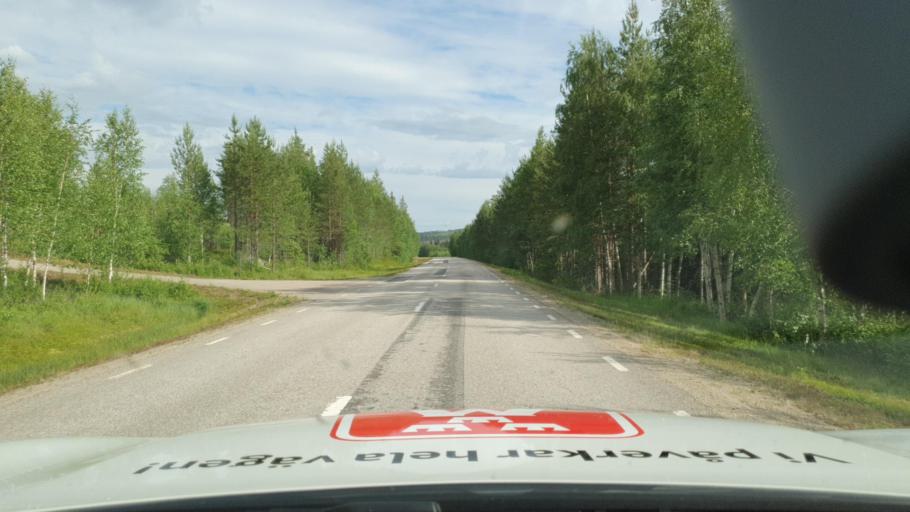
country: NO
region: Hedmark
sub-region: Trysil
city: Innbygda
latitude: 60.9413
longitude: 12.4749
